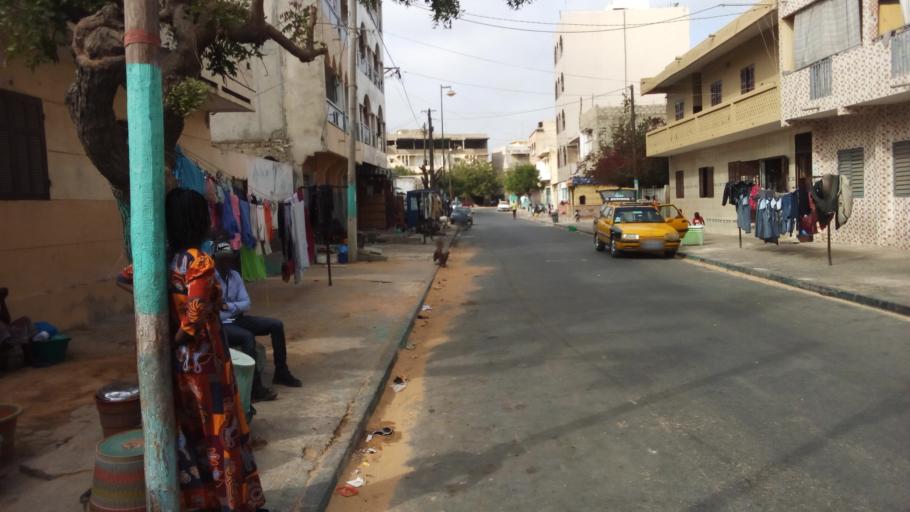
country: SN
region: Dakar
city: Dakar
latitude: 14.6904
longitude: -17.4491
